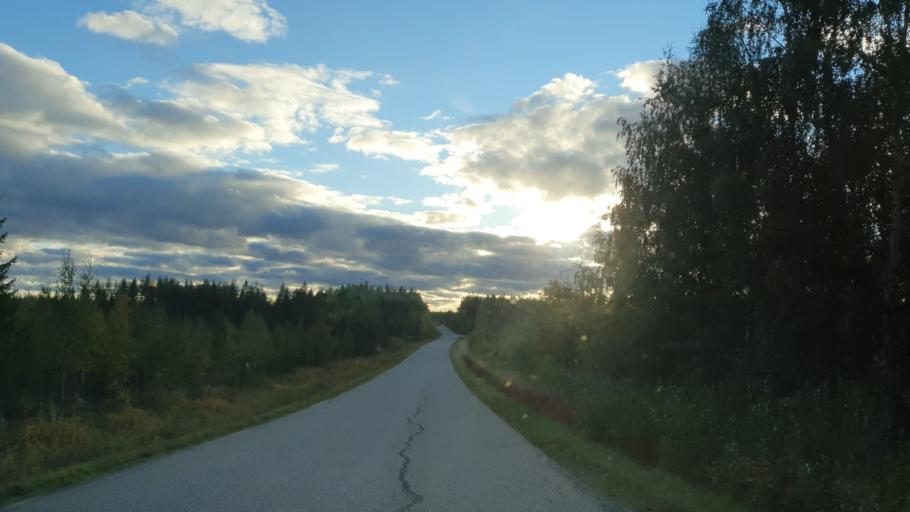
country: FI
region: Kainuu
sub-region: Kehys-Kainuu
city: Kuhmo
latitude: 63.9512
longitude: 29.7964
